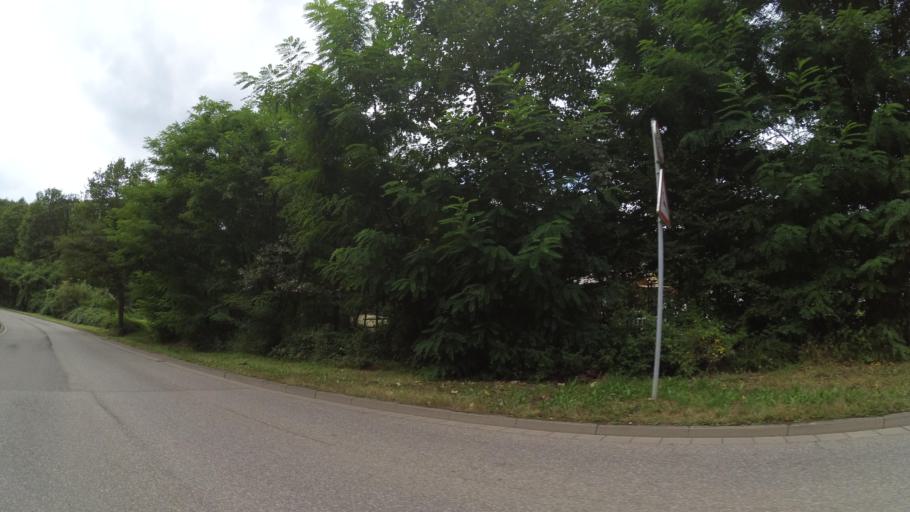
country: DE
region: Saarland
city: Puttlingen
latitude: 49.2618
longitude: 6.9042
